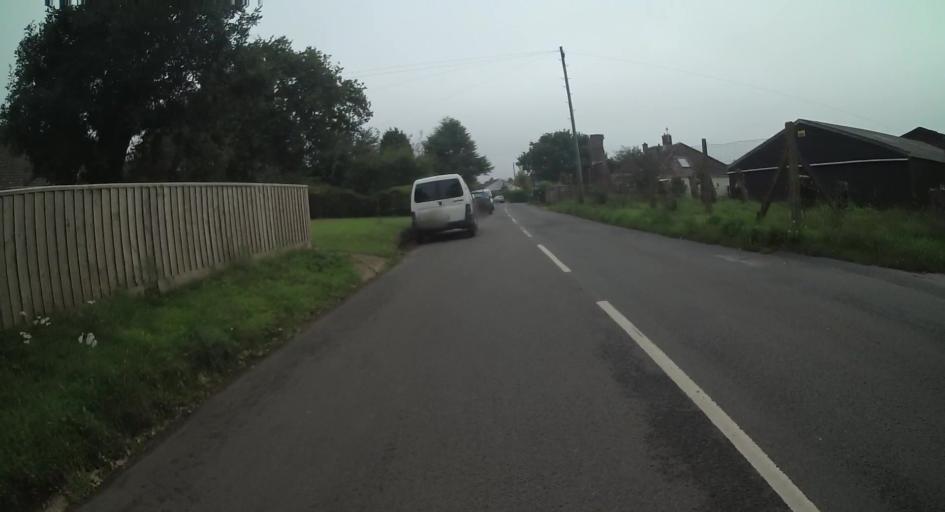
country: GB
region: England
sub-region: Isle of Wight
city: Newchurch
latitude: 50.6573
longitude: -1.1989
